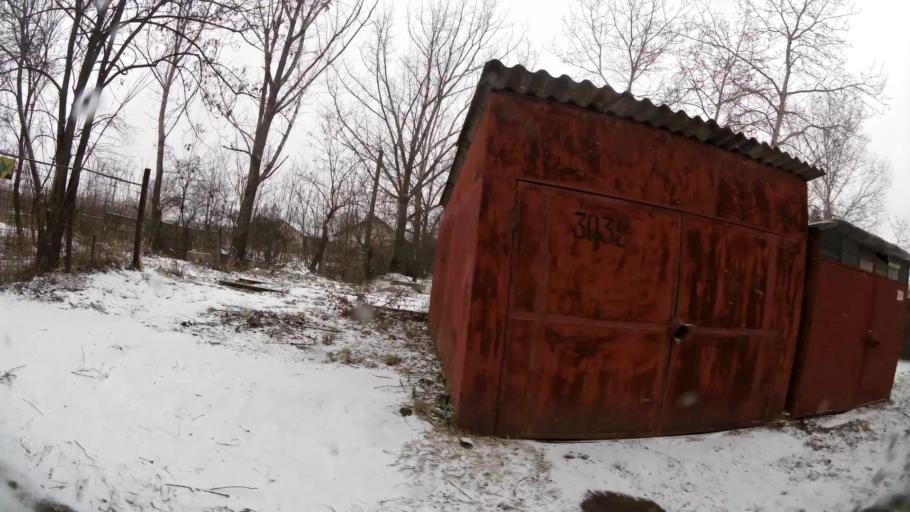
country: RO
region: Dambovita
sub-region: Municipiul Targoviste
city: Targoviste
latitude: 44.9162
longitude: 25.4608
